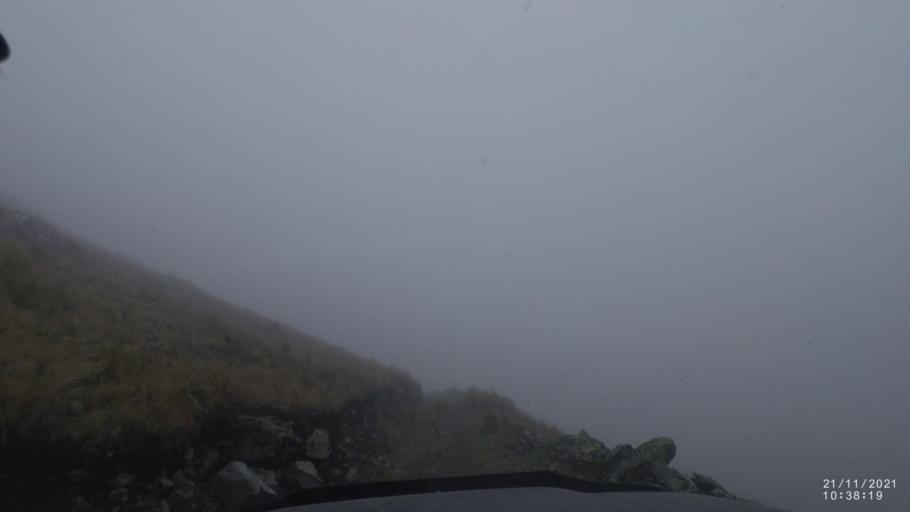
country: BO
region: Cochabamba
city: Cochabamba
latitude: -16.9682
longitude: -66.2696
